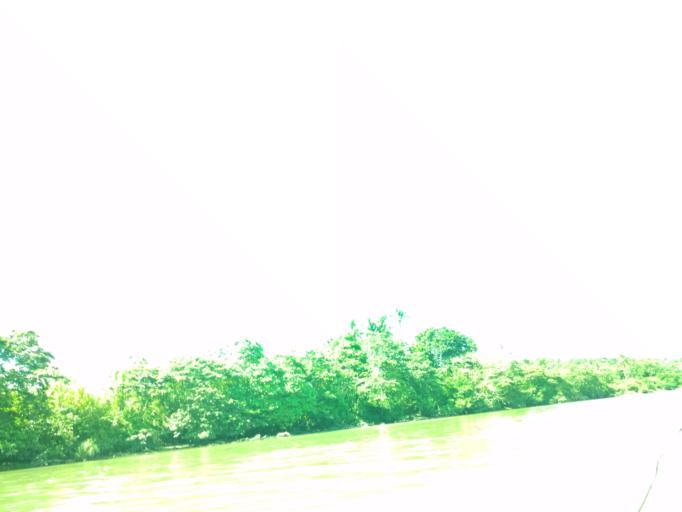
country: CO
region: Cauca
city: Timbiqui
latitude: 2.7657
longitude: -77.6631
